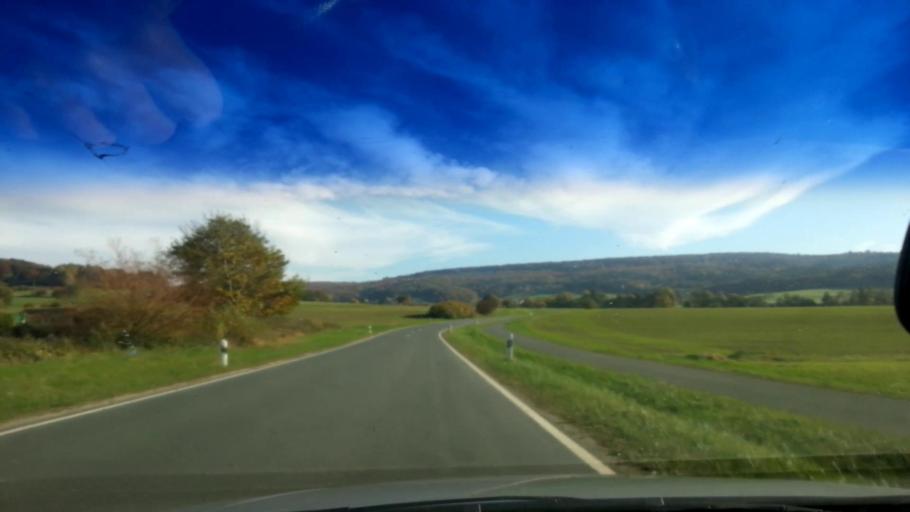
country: DE
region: Bavaria
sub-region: Upper Franconia
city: Litzendorf
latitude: 49.9069
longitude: 11.0187
